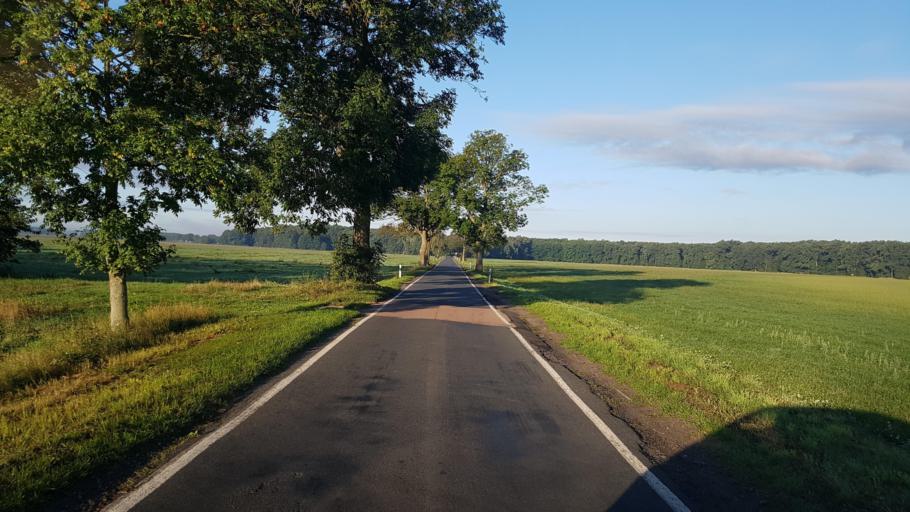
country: DE
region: Saxony-Anhalt
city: Holzdorf
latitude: 51.8265
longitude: 13.1136
